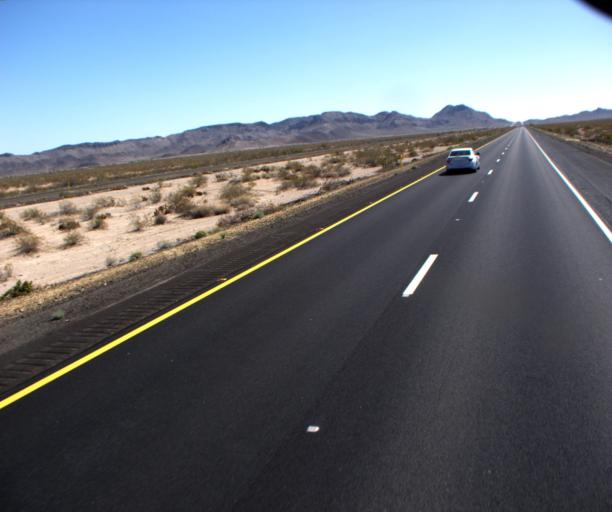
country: US
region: Arizona
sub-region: La Paz County
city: Salome
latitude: 33.6201
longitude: -113.6958
